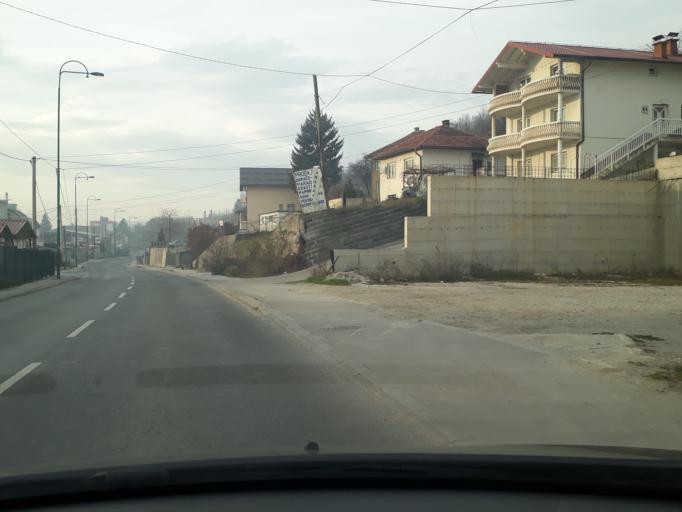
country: BA
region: Federation of Bosnia and Herzegovina
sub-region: Kanton Sarajevo
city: Sarajevo
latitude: 43.8536
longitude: 18.3315
